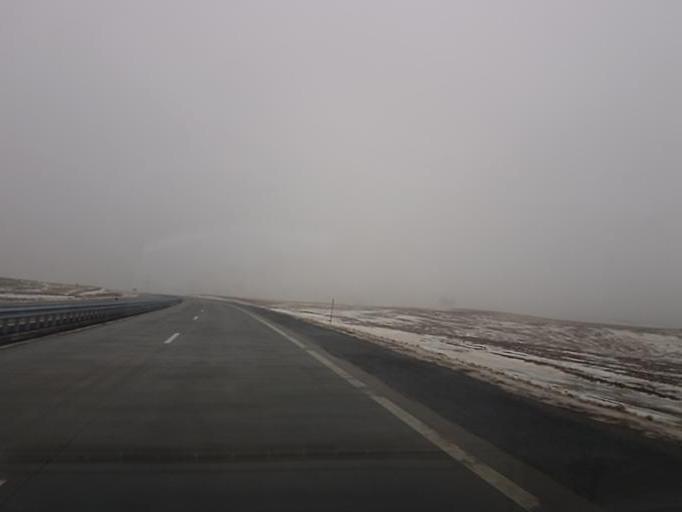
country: BY
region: Minsk
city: Atolina
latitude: 53.7589
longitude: 27.4043
